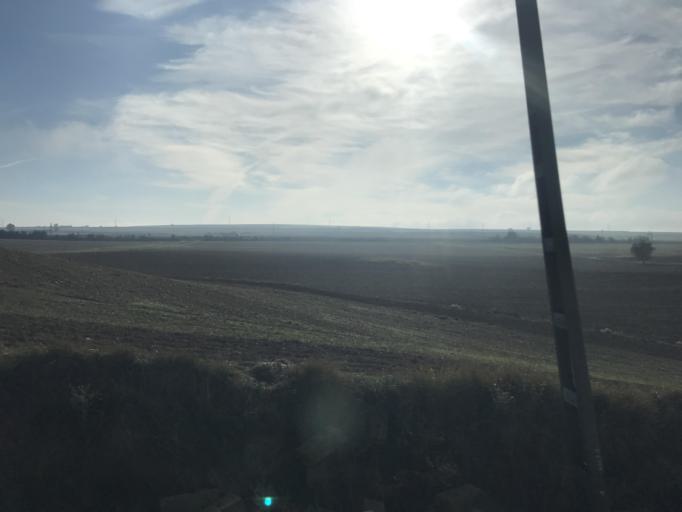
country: ES
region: Castille and Leon
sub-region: Provincia de Burgos
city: Aguilar de Bureba
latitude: 42.5894
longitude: -3.2972
